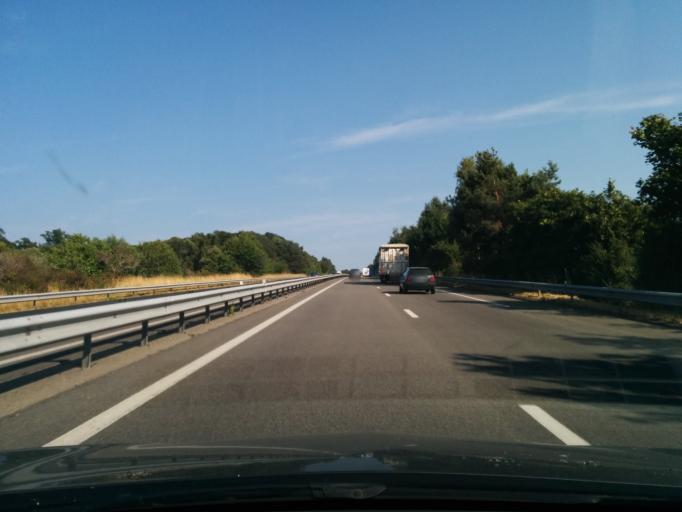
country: FR
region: Limousin
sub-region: Departement de la Haute-Vienne
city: Saint-Germain-les-Belles
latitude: 45.5808
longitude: 1.4786
